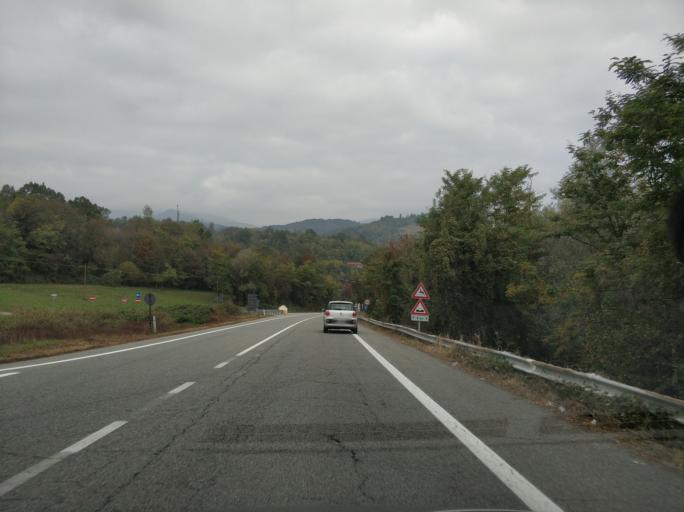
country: IT
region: Piedmont
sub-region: Provincia di Torino
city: Baldissero Canavese
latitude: 45.4096
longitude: 7.7541
